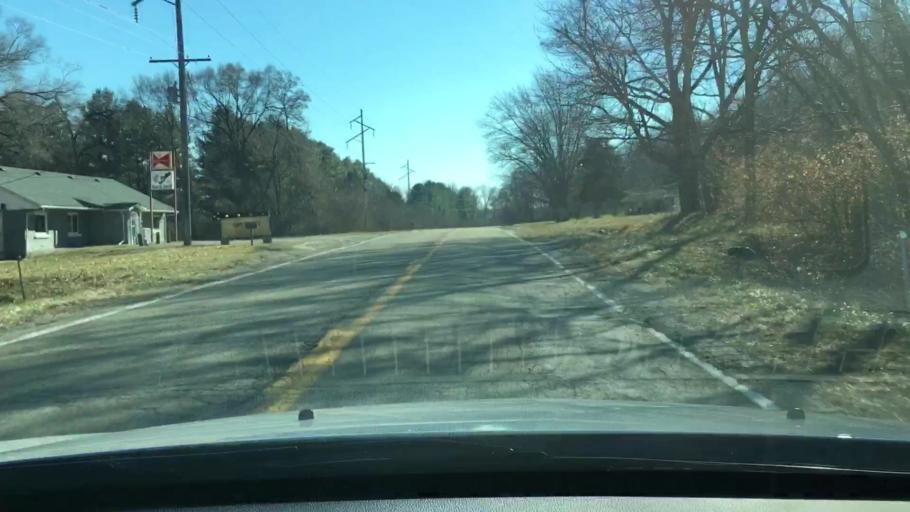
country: US
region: Illinois
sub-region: Fulton County
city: Astoria
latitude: 40.2060
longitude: -90.2039
